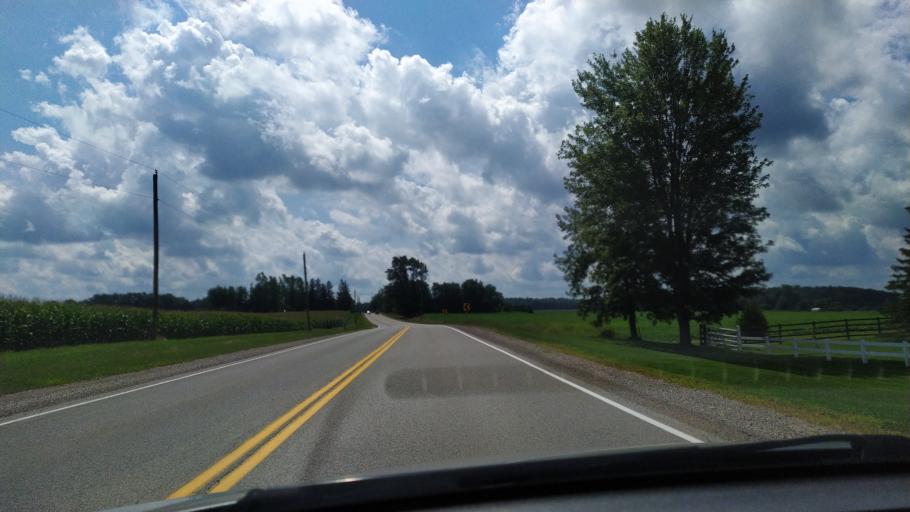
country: CA
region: Ontario
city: London
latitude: 43.0599
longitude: -81.3320
